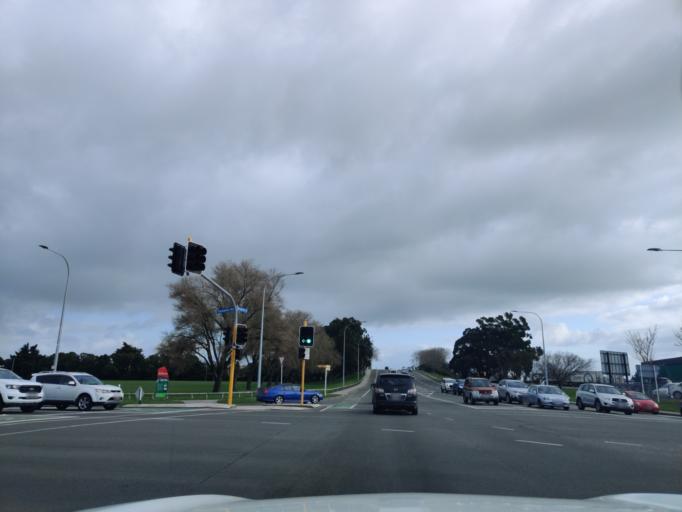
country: NZ
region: Manawatu-Wanganui
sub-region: Palmerston North City
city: Palmerston North
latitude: -40.3436
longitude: 175.6014
